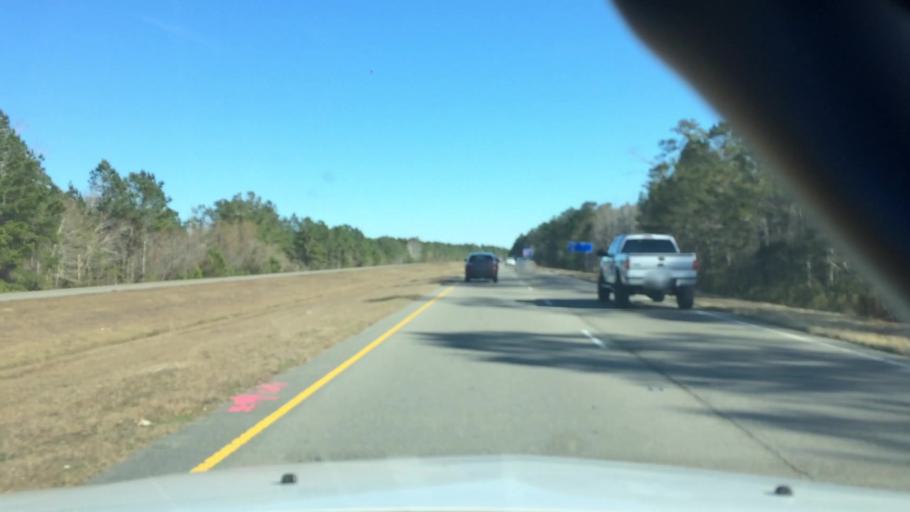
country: US
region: North Carolina
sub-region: Brunswick County
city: Shallotte
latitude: 33.9651
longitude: -78.4147
